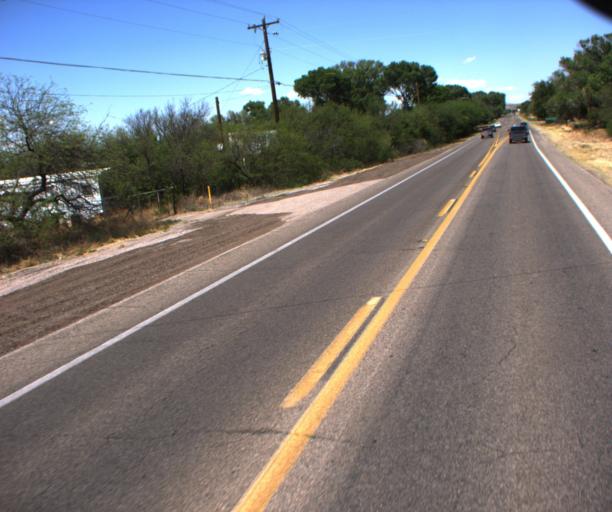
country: US
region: Arizona
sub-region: Cochise County
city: Saint David
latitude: 31.8884
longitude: -110.2135
